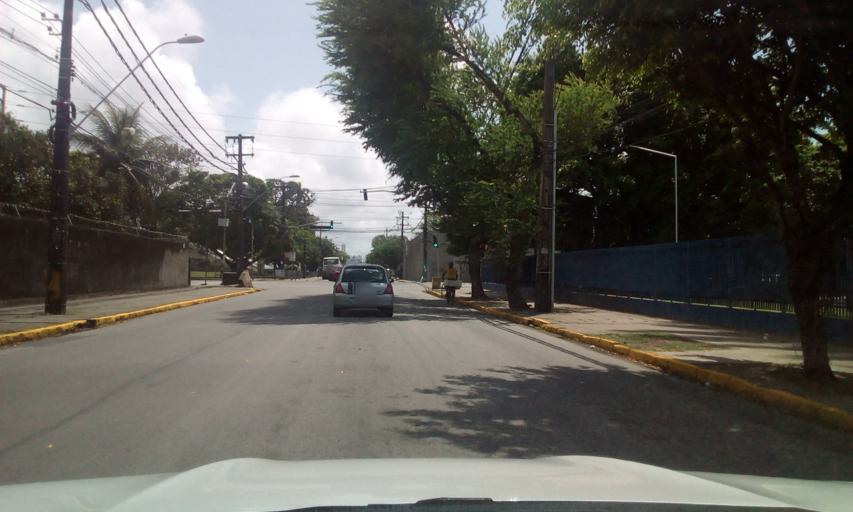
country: BR
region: Pernambuco
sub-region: Recife
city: Recife
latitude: -8.0611
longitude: -34.9260
